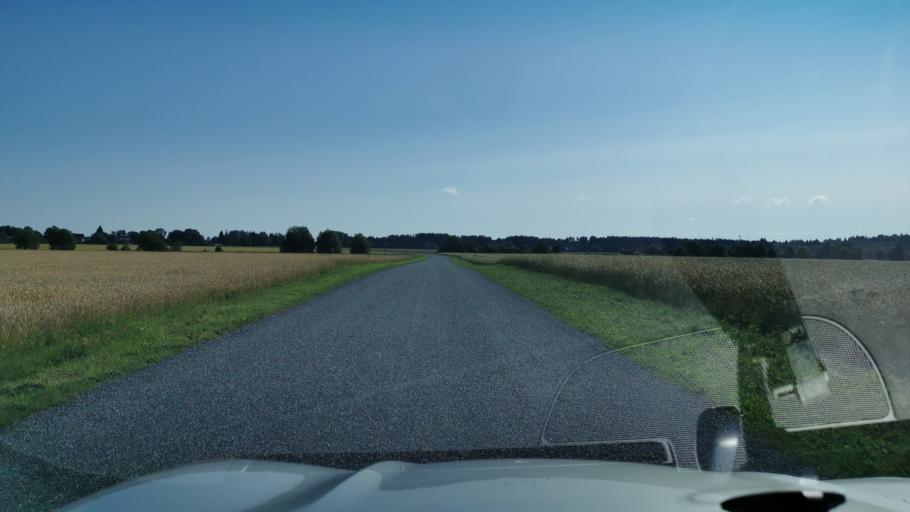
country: EE
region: Harju
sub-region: Paldiski linn
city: Paldiski
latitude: 59.2130
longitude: 24.0319
